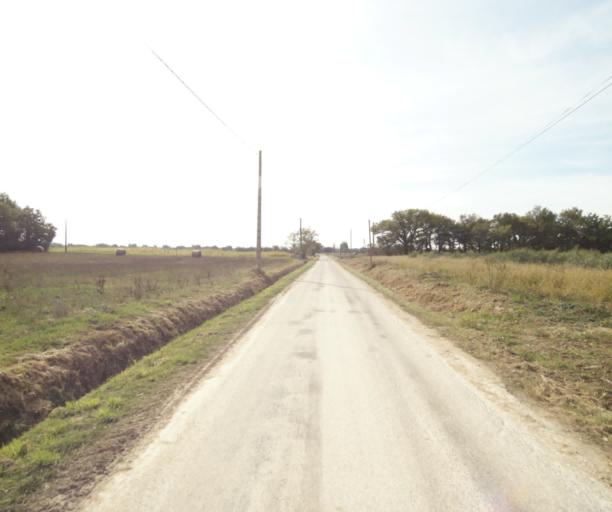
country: FR
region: Midi-Pyrenees
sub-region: Departement du Tarn-et-Garonne
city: Labastide-Saint-Pierre
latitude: 43.8922
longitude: 1.3564
